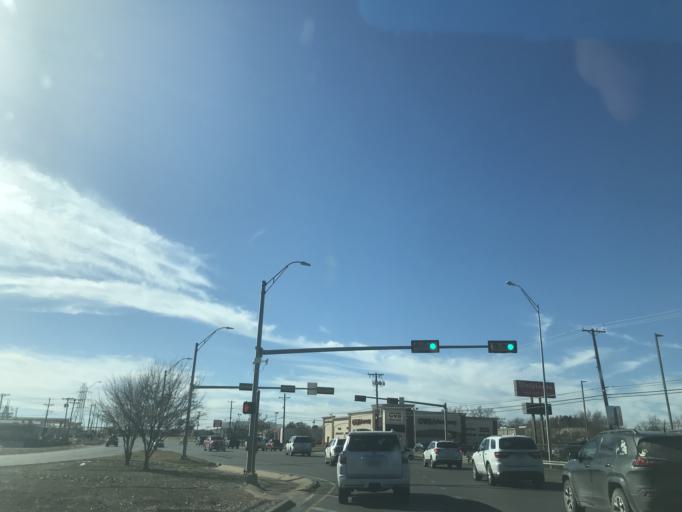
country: US
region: Texas
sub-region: Erath County
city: Stephenville
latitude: 32.2074
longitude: -98.2300
